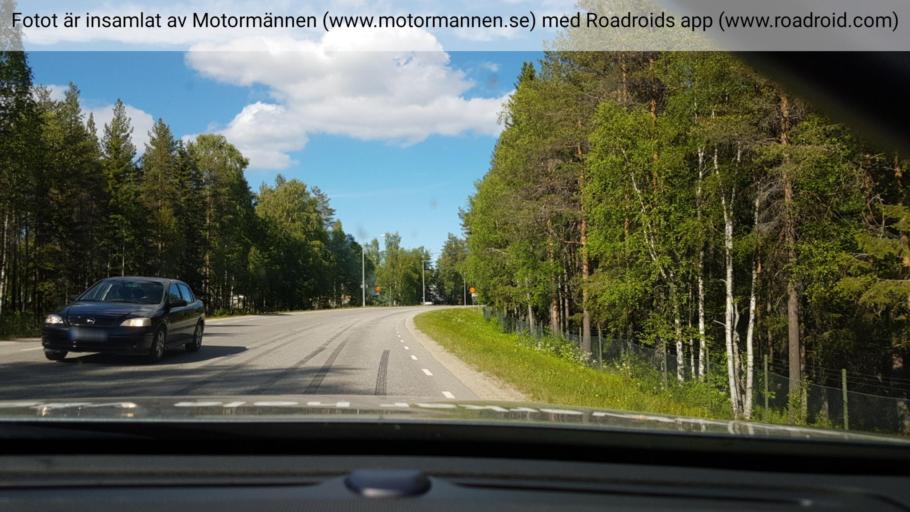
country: SE
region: Vaesterbotten
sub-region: Lycksele Kommun
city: Lycksele
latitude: 64.5823
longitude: 18.6587
